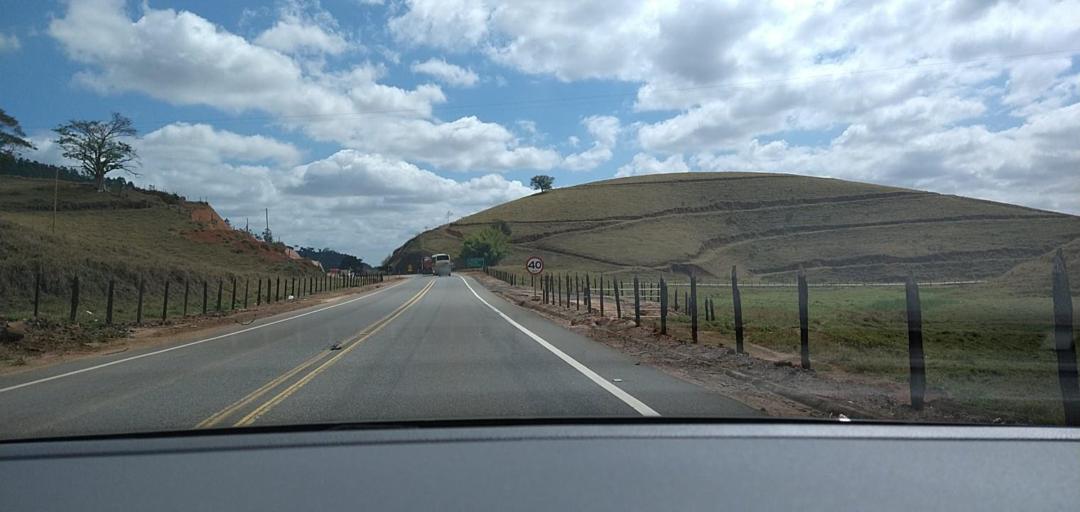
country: BR
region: Minas Gerais
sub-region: Ponte Nova
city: Ponte Nova
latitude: -20.4846
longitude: -42.8787
